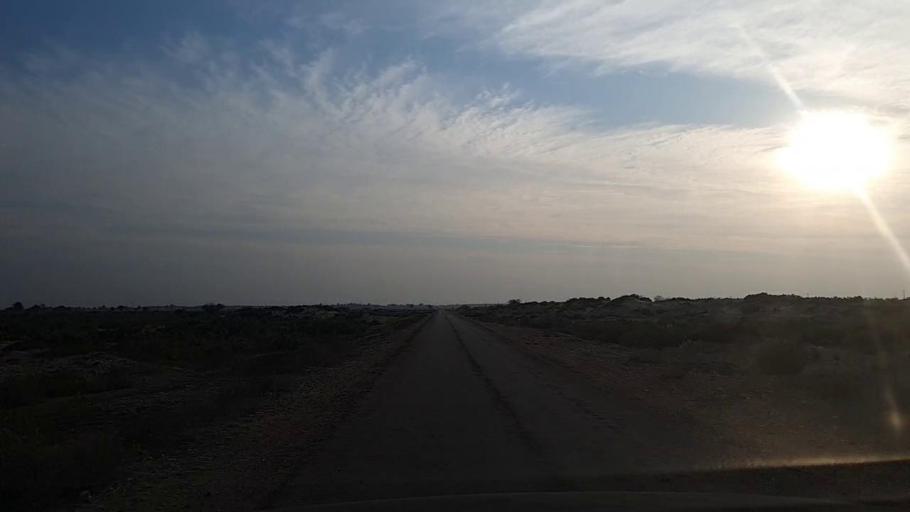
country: PK
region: Sindh
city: Jam Sahib
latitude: 26.4070
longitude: 68.5089
